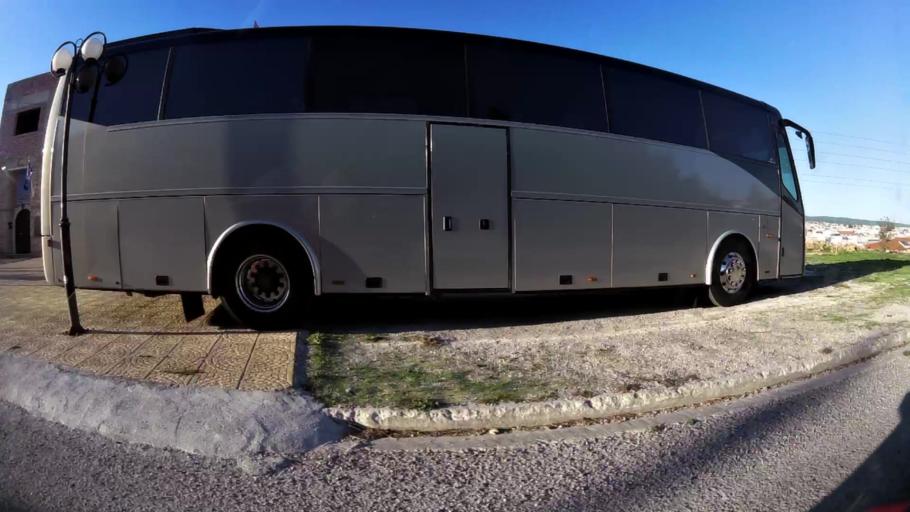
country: GR
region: Attica
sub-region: Nomarchia Anatolikis Attikis
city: Acharnes
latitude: 38.0840
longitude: 23.7233
